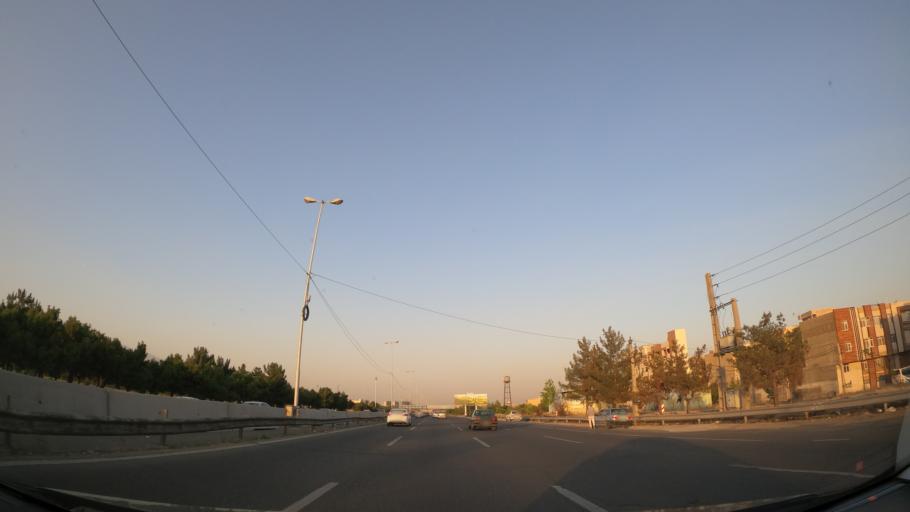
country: IR
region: Tehran
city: Tehran
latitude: 35.7156
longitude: 51.2775
